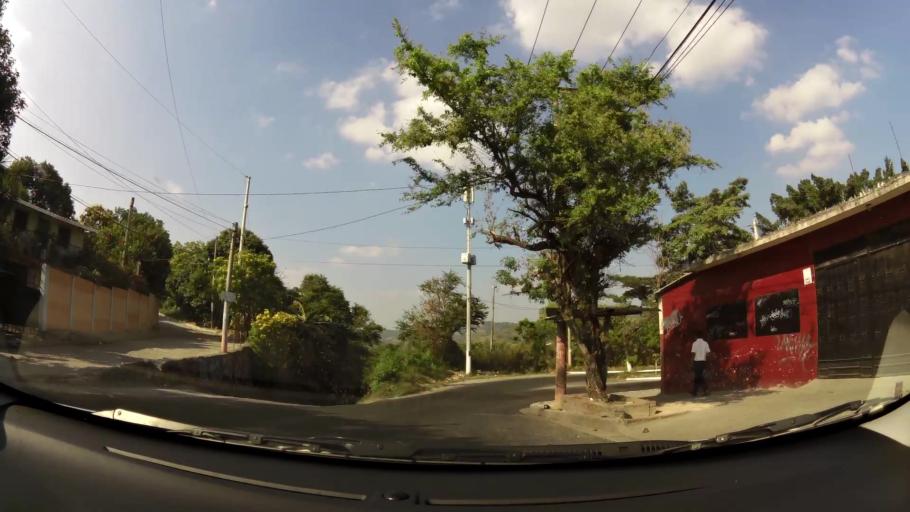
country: SV
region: San Salvador
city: Ilopango
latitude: 13.7161
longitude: -89.1073
